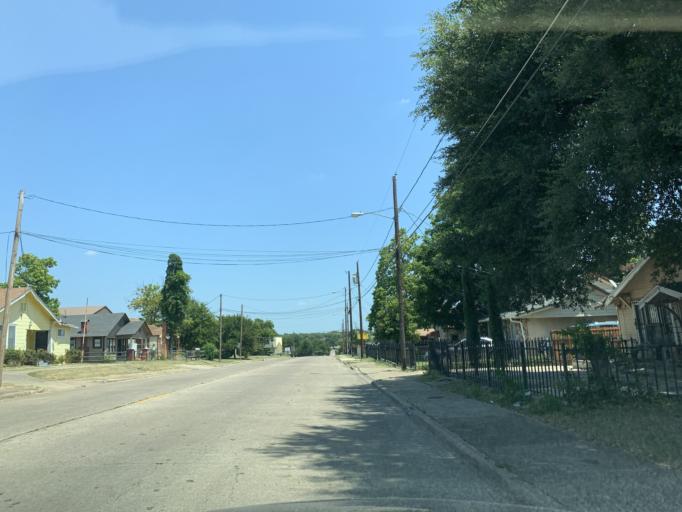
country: US
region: Texas
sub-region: Dallas County
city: Dallas
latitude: 32.6939
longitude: -96.8015
